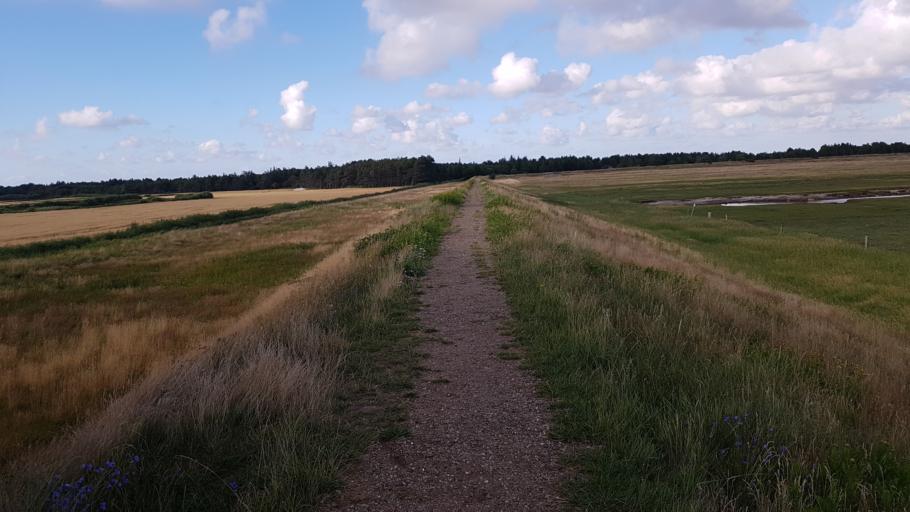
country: DE
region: Schleswig-Holstein
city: List
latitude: 55.0792
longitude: 8.5281
